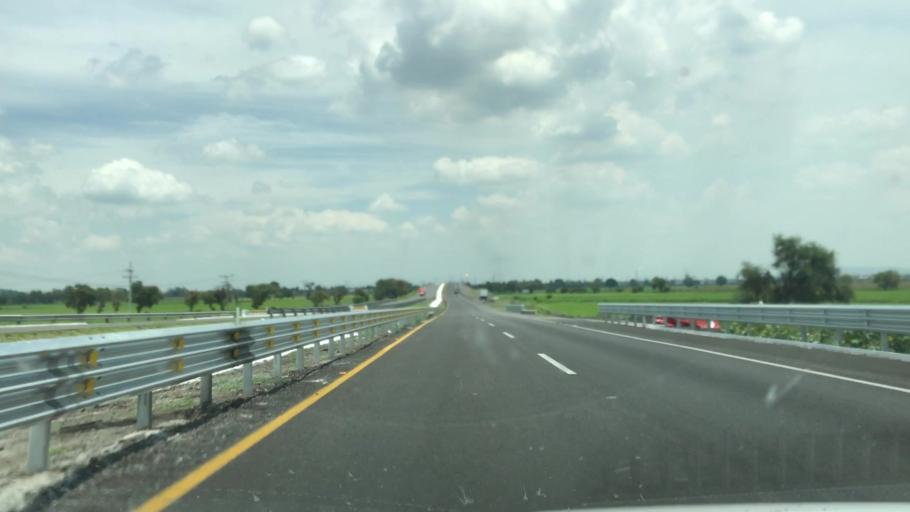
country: MX
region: Guanajuato
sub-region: Salamanca
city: San Vicente de Flores
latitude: 20.6117
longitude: -101.2207
